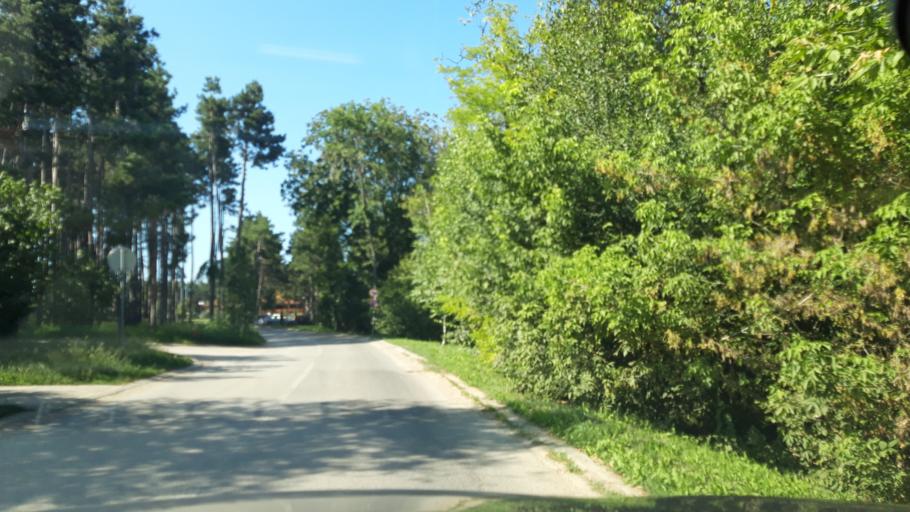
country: RS
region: Autonomna Pokrajina Vojvodina
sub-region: Sremski Okrug
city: Ruma
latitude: 45.0324
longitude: 19.8199
